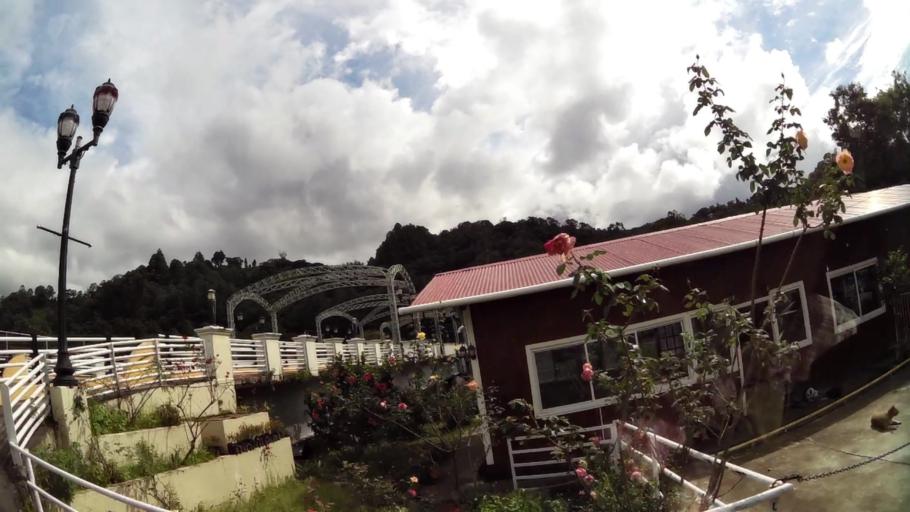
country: PA
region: Chiriqui
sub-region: Distrito Boquete
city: Boquete
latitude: 8.7763
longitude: -82.4308
